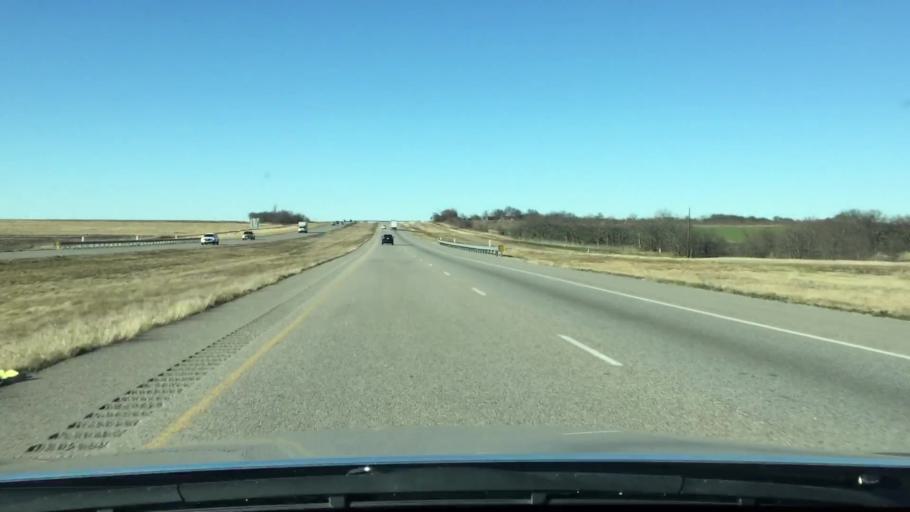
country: US
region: Texas
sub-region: Hill County
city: Itasca
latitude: 32.1135
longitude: -97.1140
